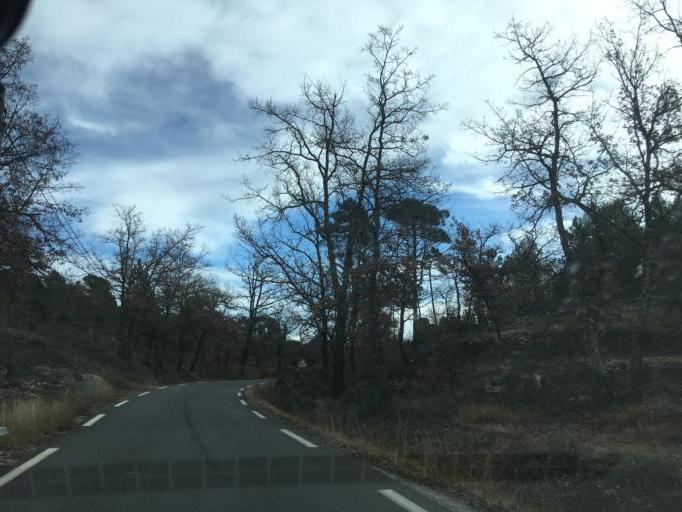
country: FR
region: Provence-Alpes-Cote d'Azur
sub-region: Departement du Var
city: Bras
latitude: 43.4537
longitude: 5.9715
